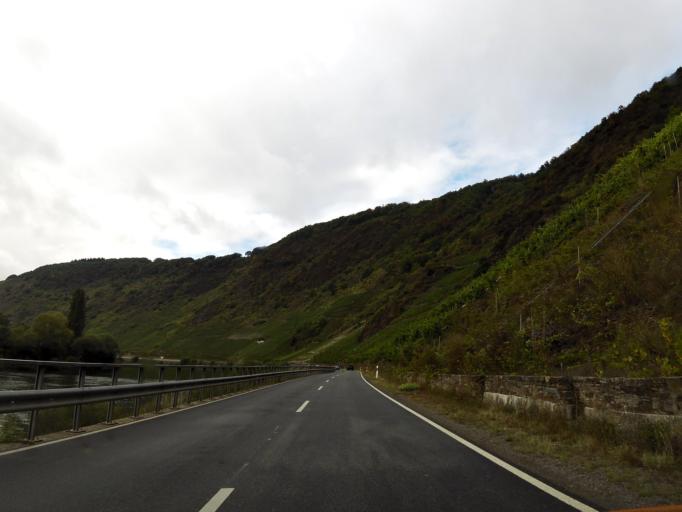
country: DE
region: Rheinland-Pfalz
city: Ernst
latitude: 50.1448
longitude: 7.2344
